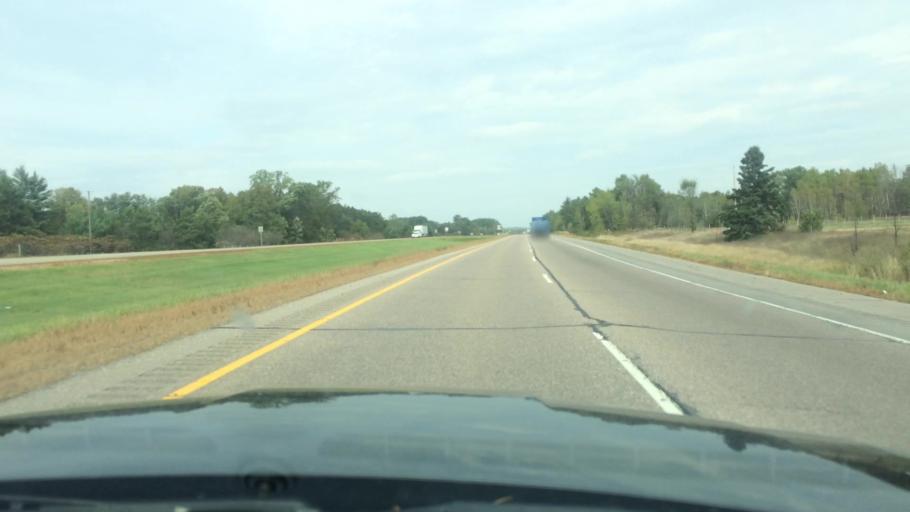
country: US
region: Wisconsin
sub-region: Marathon County
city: Mosinee
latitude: 44.6625
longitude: -89.6428
